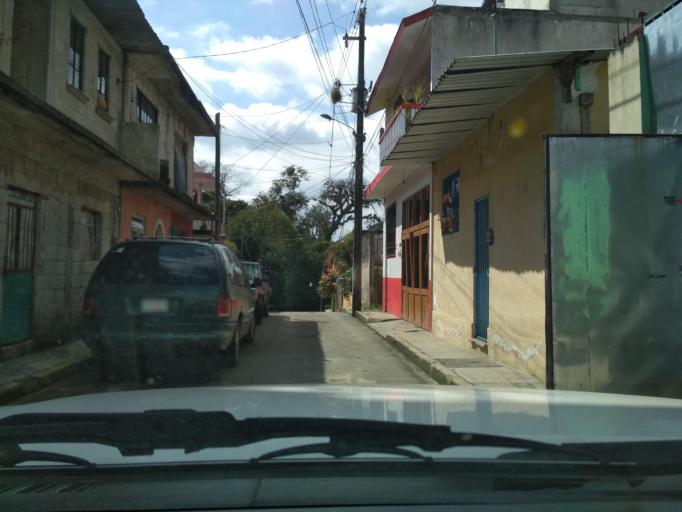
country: MX
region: Veracruz
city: Coatepec
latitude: 19.4489
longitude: -96.9484
